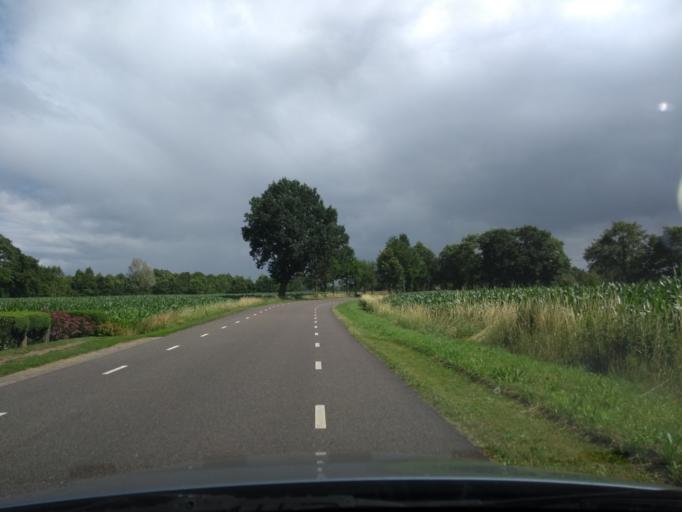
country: NL
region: Overijssel
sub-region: Gemeente Twenterand
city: Den Ham
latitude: 52.4488
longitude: 6.4194
